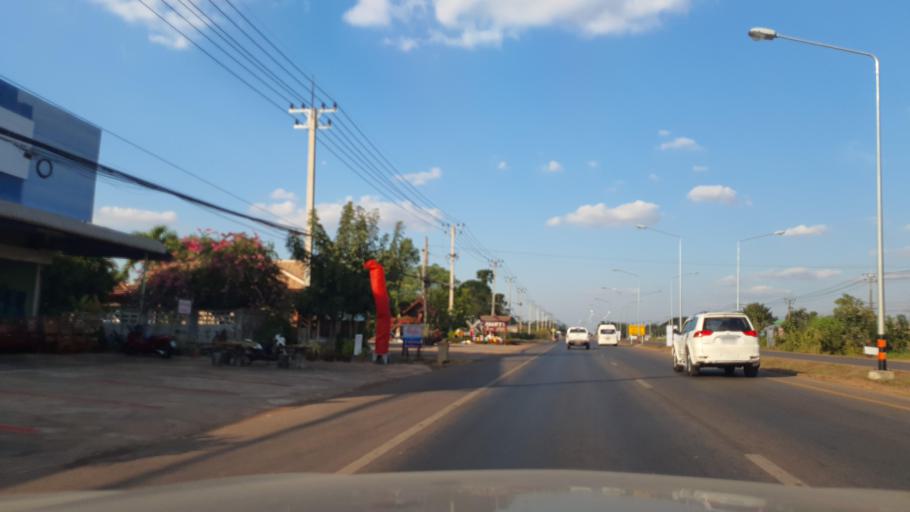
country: TH
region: Sakon Nakhon
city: Sakon Nakhon
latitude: 17.2224
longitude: 104.1053
